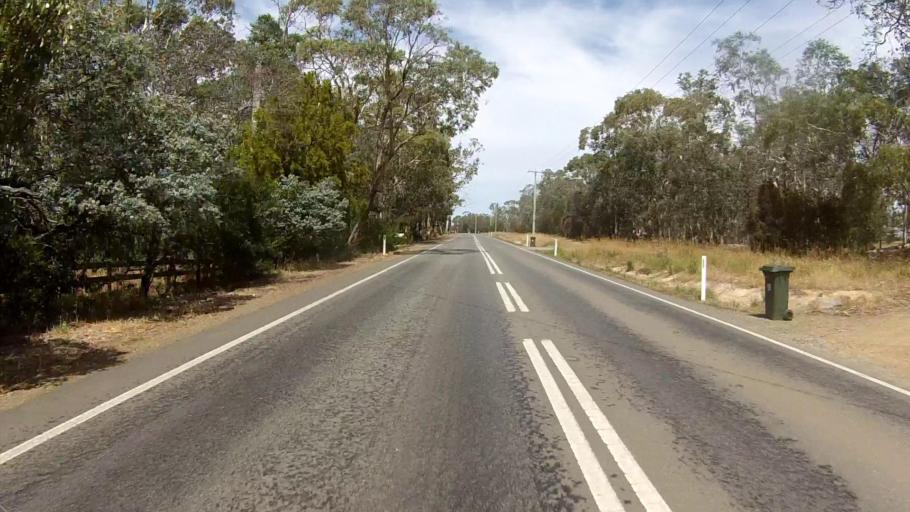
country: AU
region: Tasmania
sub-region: Clarence
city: Sandford
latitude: -42.9697
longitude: 147.5033
